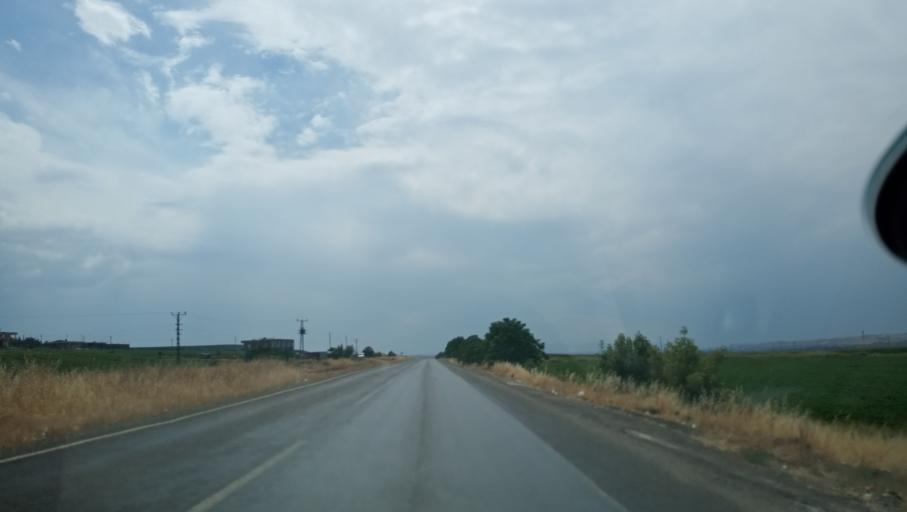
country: TR
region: Diyarbakir
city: Kerh
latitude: 37.8262
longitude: 40.5338
